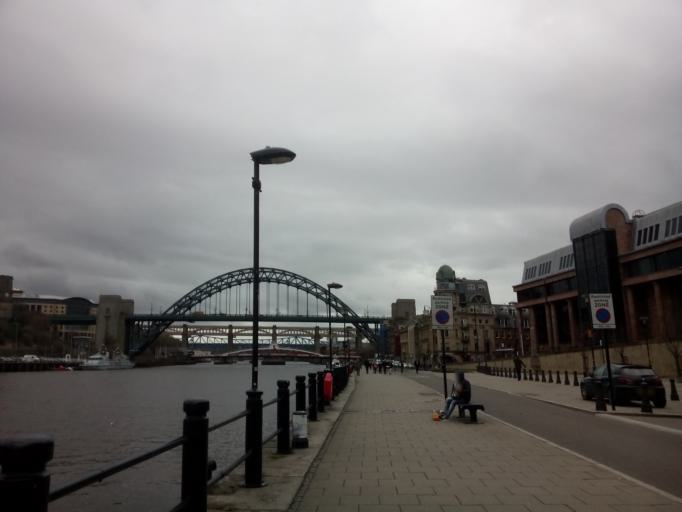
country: GB
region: England
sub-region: Gateshead
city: Gateshead
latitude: 54.9699
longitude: -1.6014
